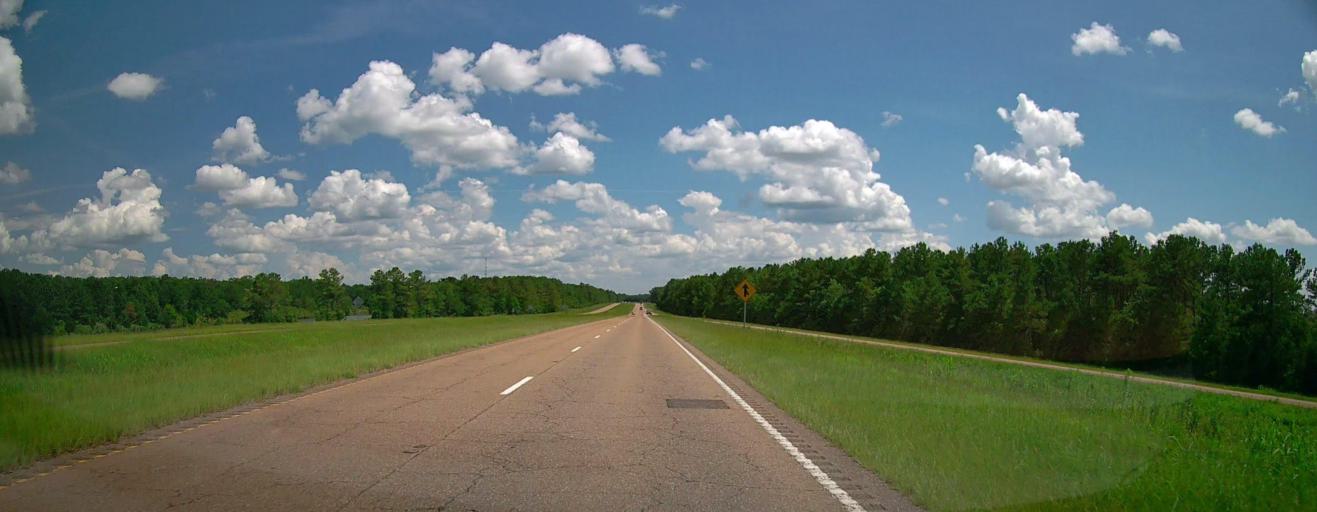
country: US
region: Mississippi
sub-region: Monroe County
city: Aberdeen
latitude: 33.8391
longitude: -88.5913
